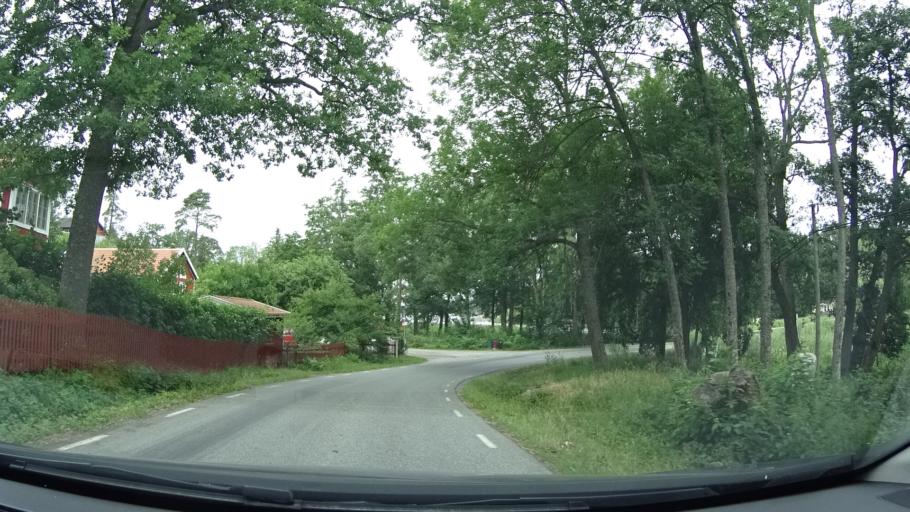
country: SE
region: Stockholm
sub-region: Varmdo Kommun
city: Mortnas
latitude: 59.3701
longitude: 18.4660
